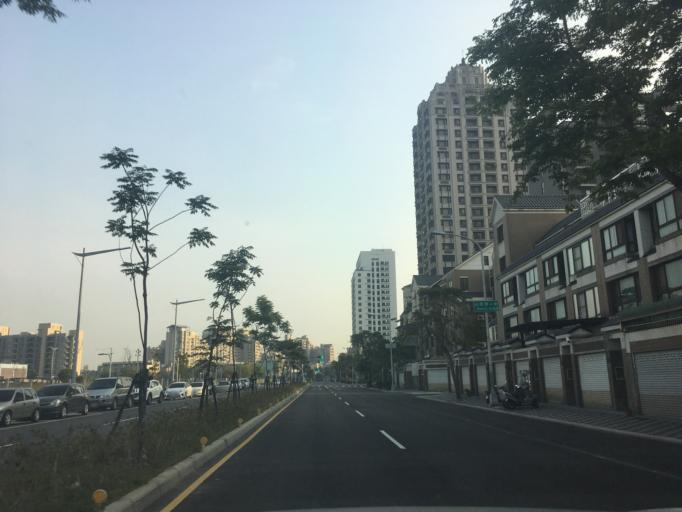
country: TW
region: Taiwan
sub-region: Taichung City
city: Taichung
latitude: 24.1842
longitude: 120.6822
